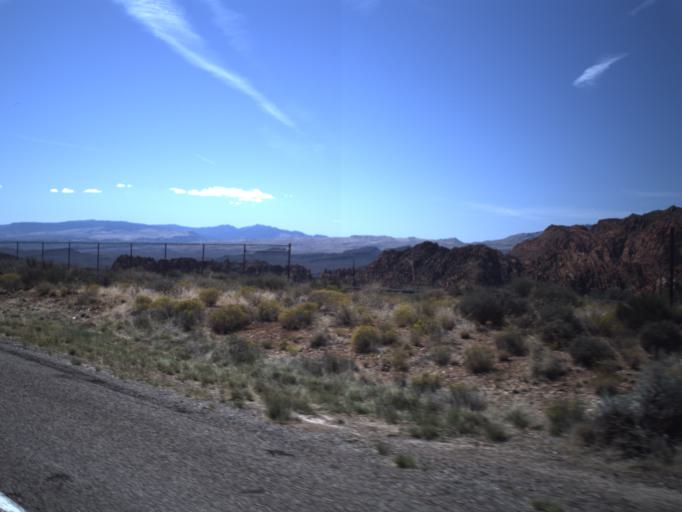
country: US
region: Utah
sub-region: Washington County
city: Ivins
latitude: 37.2176
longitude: -113.6332
